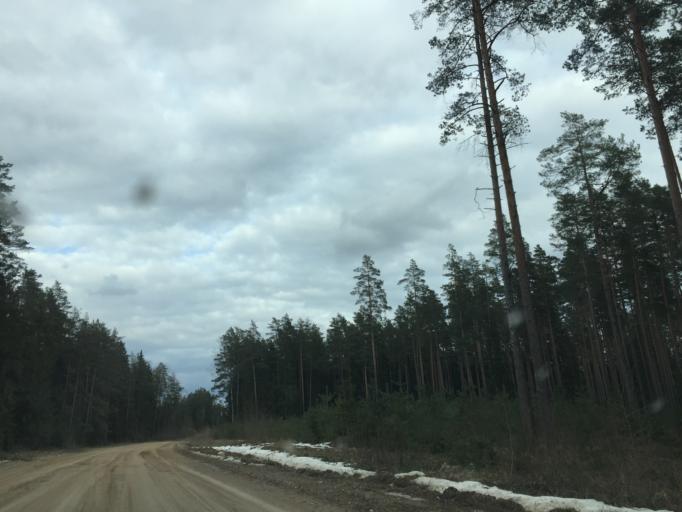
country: LV
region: Lielvarde
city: Lielvarde
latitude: 56.5401
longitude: 24.8335
